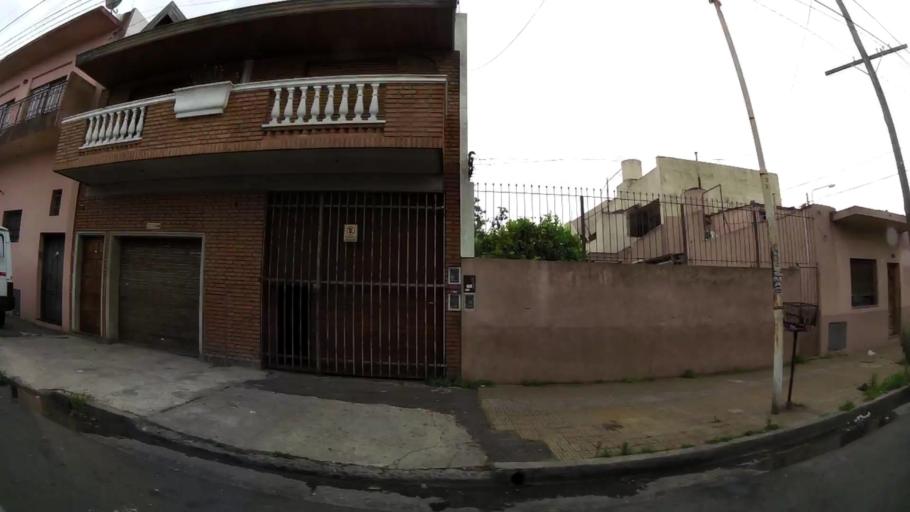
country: AR
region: Buenos Aires
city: San Justo
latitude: -34.6616
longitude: -58.5251
